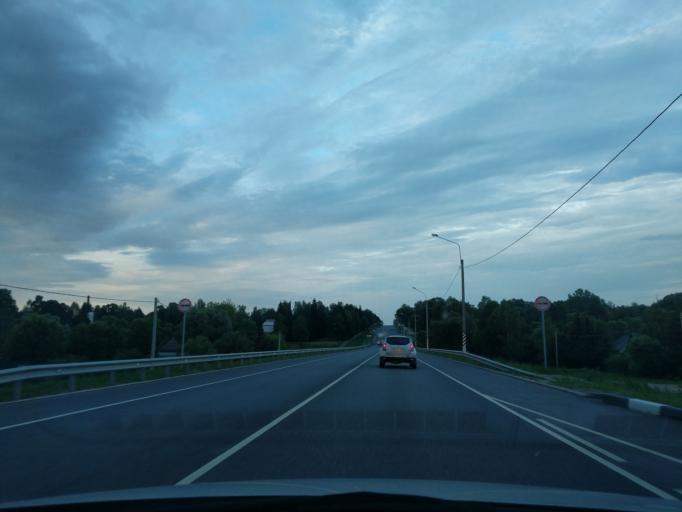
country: RU
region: Kaluga
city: Kudinovo
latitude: 54.9755
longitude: 36.1616
